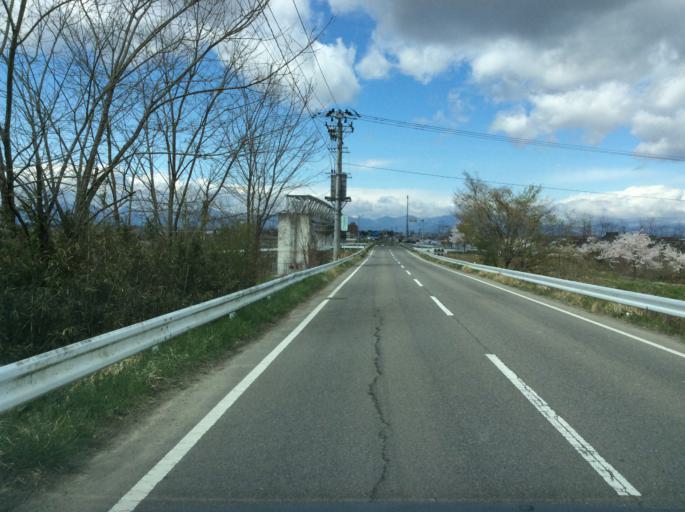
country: JP
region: Fukushima
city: Koriyama
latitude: 37.3558
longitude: 140.3996
